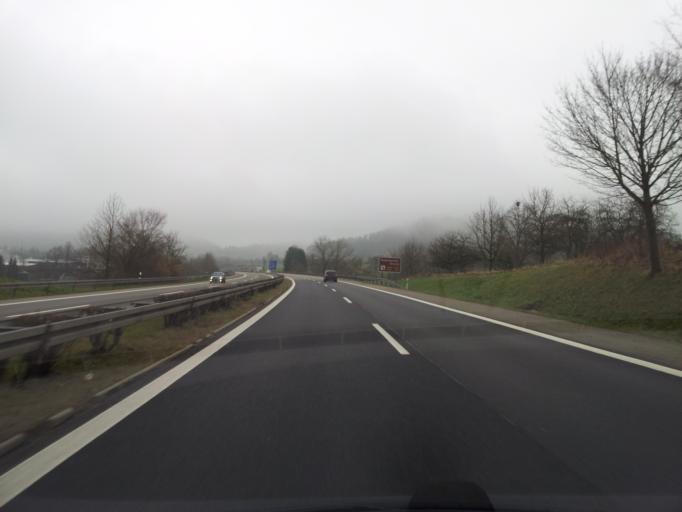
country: DE
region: Baden-Wuerttemberg
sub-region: Freiburg Region
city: Hilzingen
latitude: 47.7553
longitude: 8.7857
